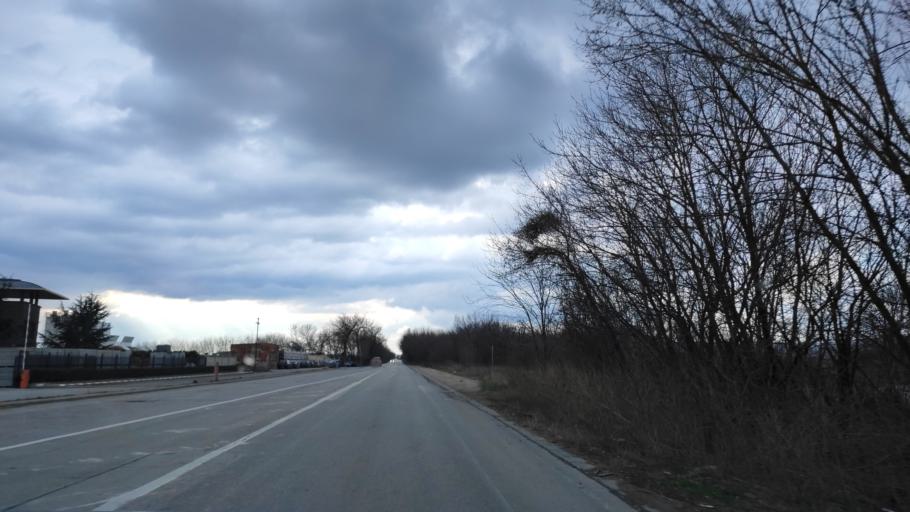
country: BG
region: Varna
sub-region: Obshtina Aksakovo
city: Aksakovo
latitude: 43.2282
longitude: 27.8438
